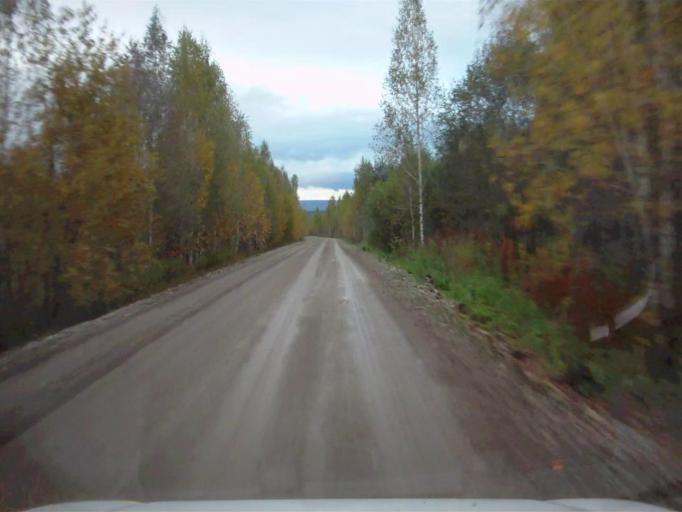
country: RU
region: Sverdlovsk
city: Mikhaylovsk
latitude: 56.1942
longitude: 59.1964
